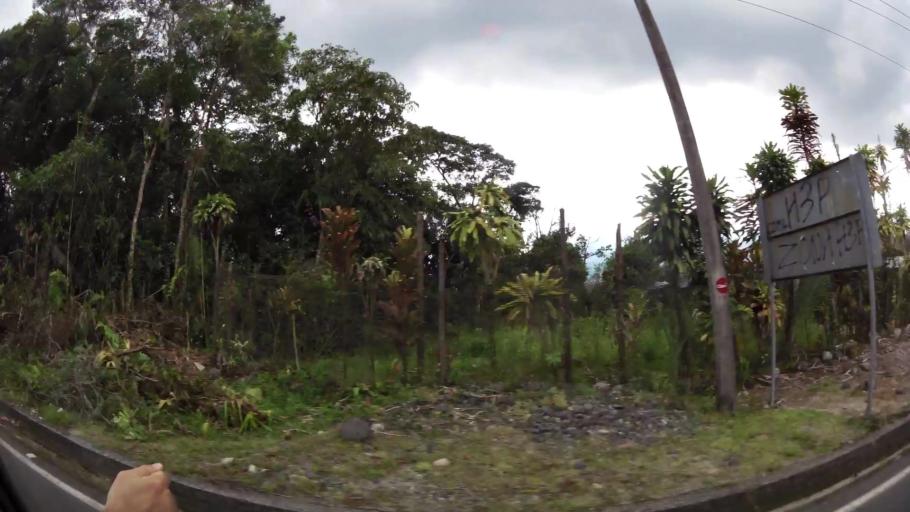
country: EC
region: Pastaza
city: Puyo
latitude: -1.4578
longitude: -78.1188
